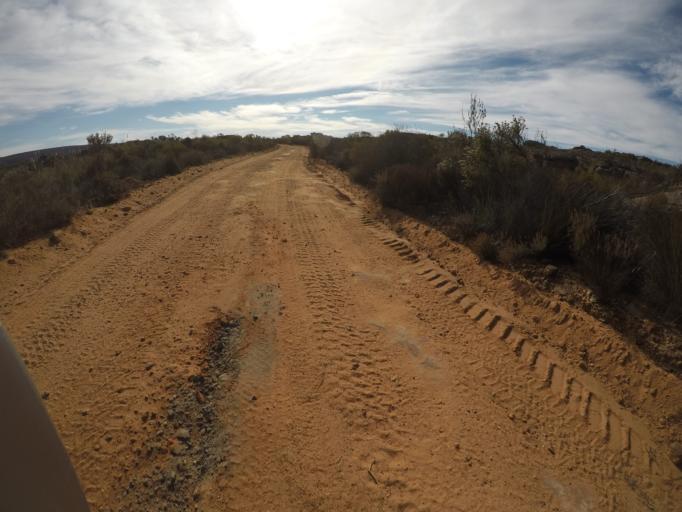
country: ZA
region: Western Cape
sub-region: West Coast District Municipality
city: Vredendal
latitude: -31.7474
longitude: 18.8236
